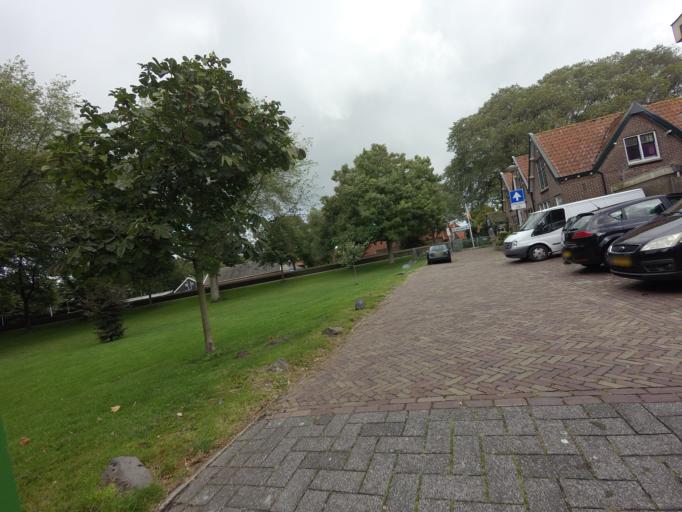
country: NL
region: North Holland
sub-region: Gemeente Enkhuizen
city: Enkhuizen
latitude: 52.7066
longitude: 5.2961
